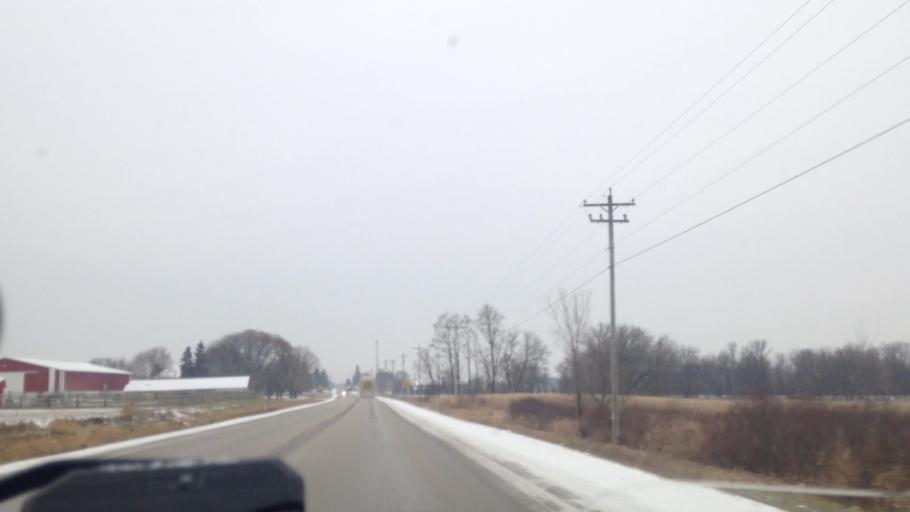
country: US
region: Wisconsin
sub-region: Dodge County
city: Mayville
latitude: 43.4088
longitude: -88.5421
